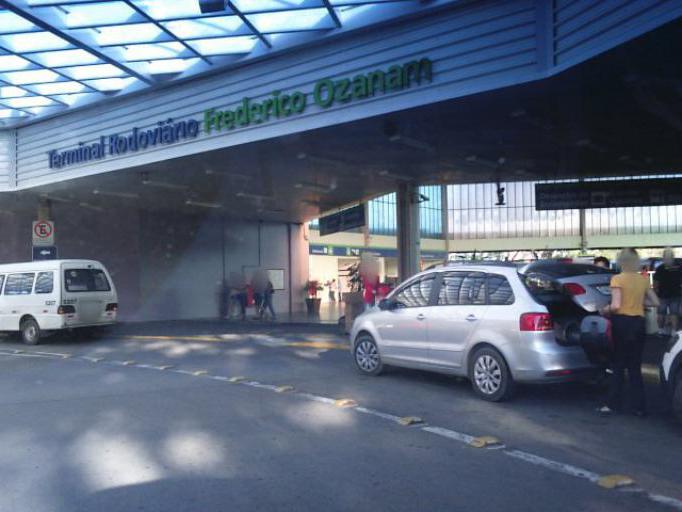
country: BR
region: Sao Paulo
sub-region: Sao Jose Dos Campos
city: Sao Jose dos Campos
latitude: -23.1935
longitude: -45.8784
